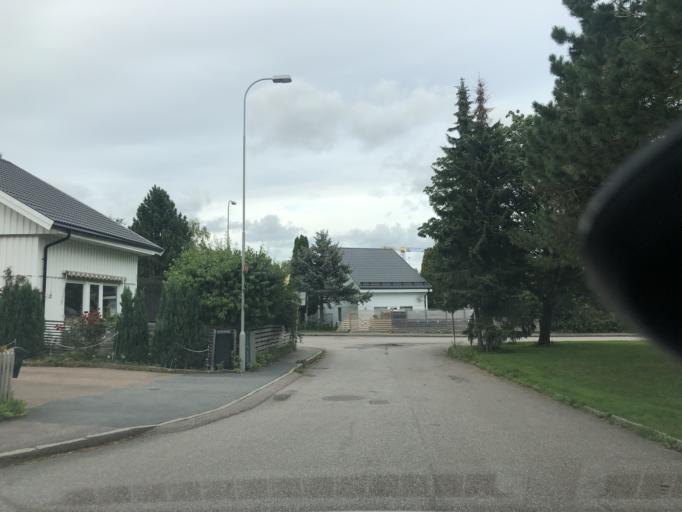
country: SE
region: Vaestra Goetaland
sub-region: Goteborg
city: Goeteborg
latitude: 57.7485
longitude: 11.9763
